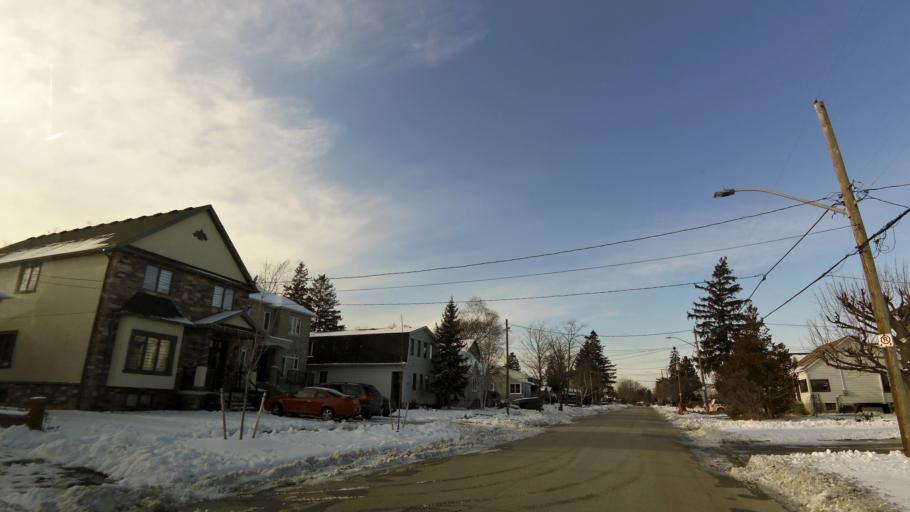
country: CA
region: Ontario
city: Etobicoke
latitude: 43.5813
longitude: -79.5699
